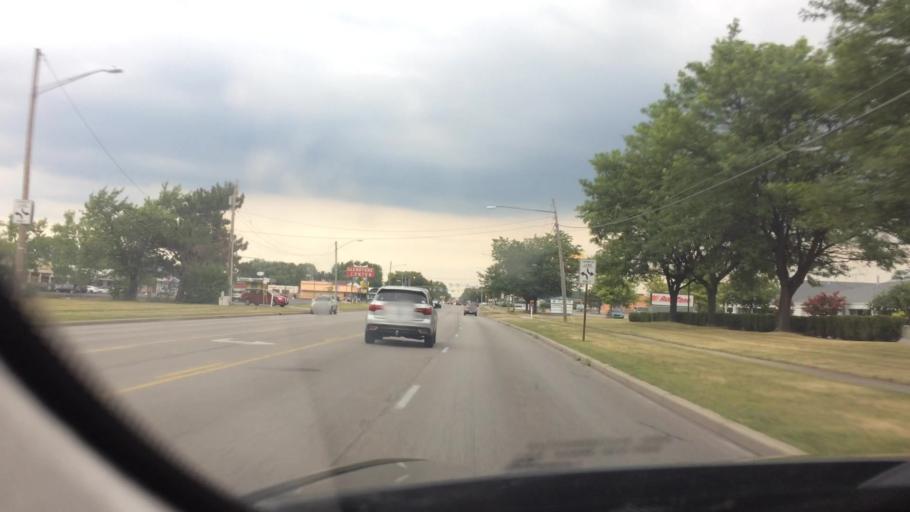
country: US
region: Ohio
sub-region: Wood County
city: Perrysburg
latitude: 41.6090
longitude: -83.6257
